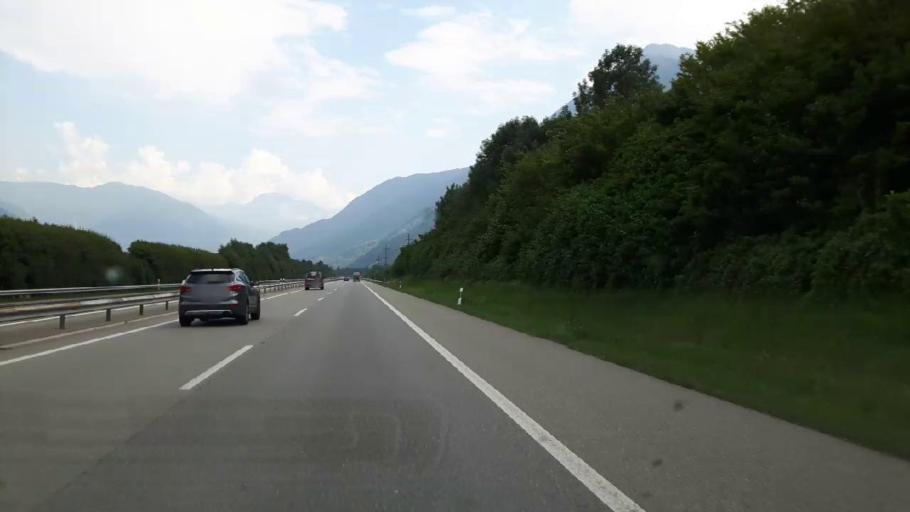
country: CH
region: Ticino
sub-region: Riviera District
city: Lodrino
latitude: 46.2920
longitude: 8.9905
